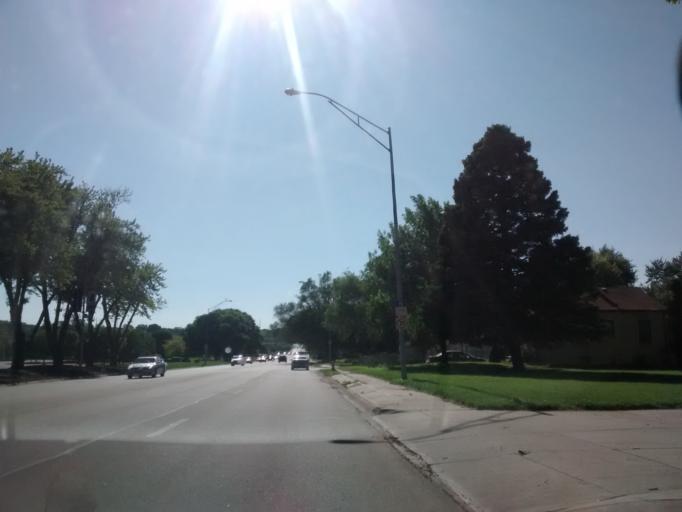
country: US
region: Nebraska
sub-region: Douglas County
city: Ralston
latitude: 41.2488
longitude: -96.0171
